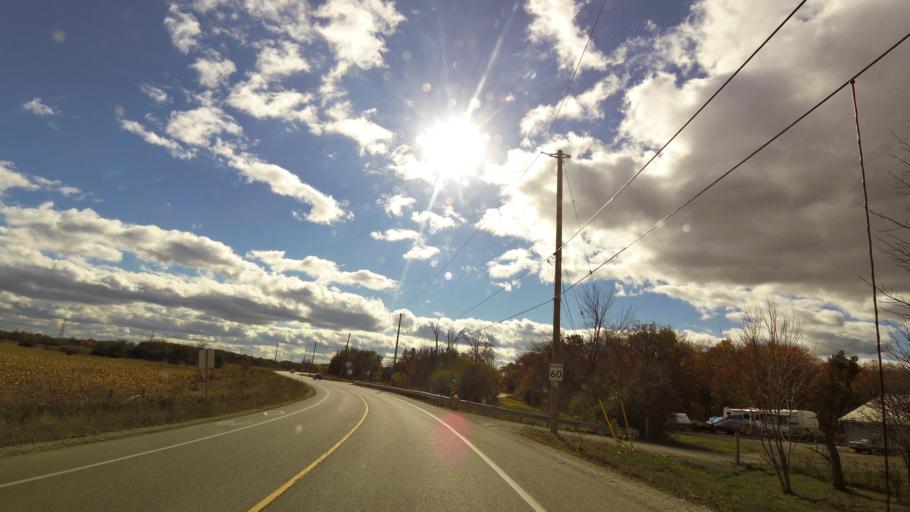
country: CA
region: Ontario
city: Oakville
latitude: 43.5036
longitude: -79.7676
